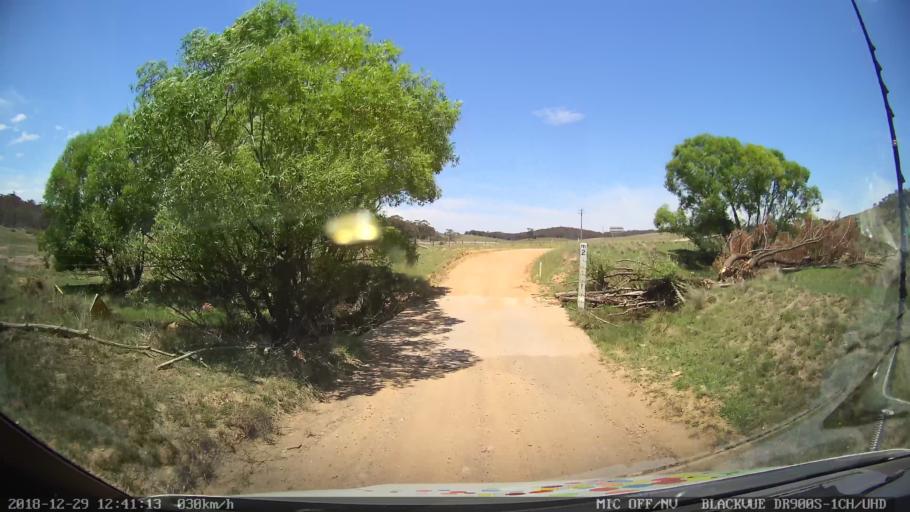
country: AU
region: Australian Capital Territory
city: Macarthur
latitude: -35.6071
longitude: 149.2228
